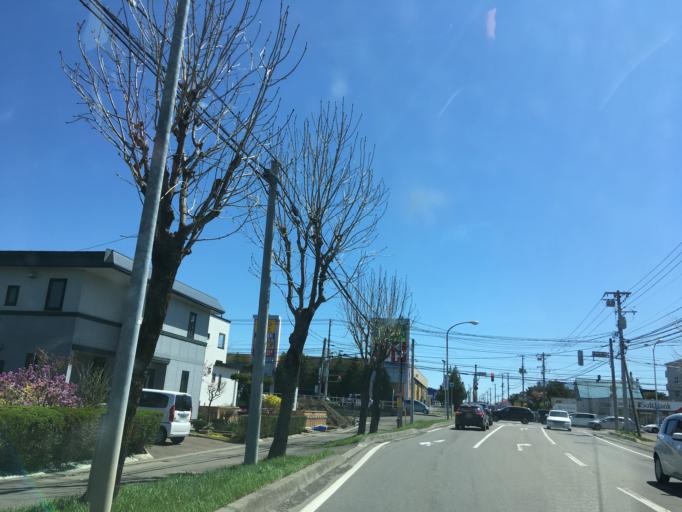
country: JP
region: Hokkaido
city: Obihiro
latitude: 42.9203
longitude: 143.1715
